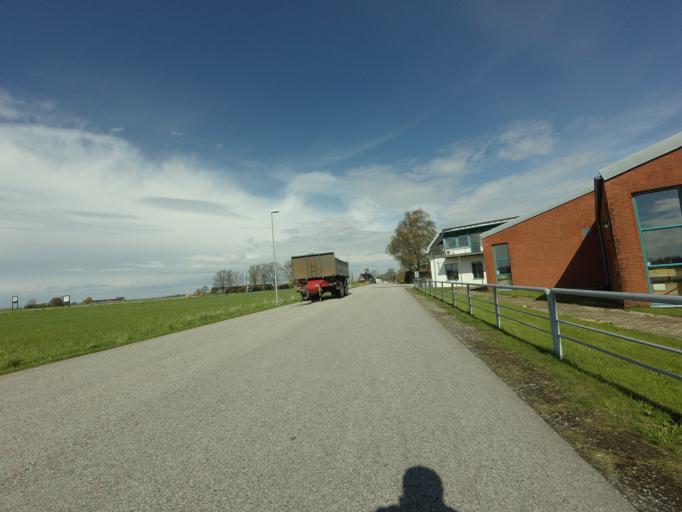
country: SE
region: Skane
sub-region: Malmo
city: Tygelsjo
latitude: 55.4926
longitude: 13.0030
